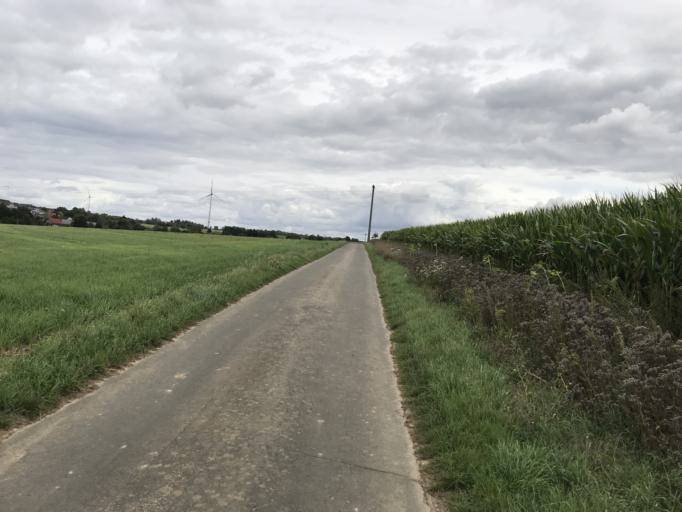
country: DE
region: Hesse
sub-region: Regierungsbezirk Giessen
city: Grunberg
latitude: 50.6317
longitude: 8.9764
